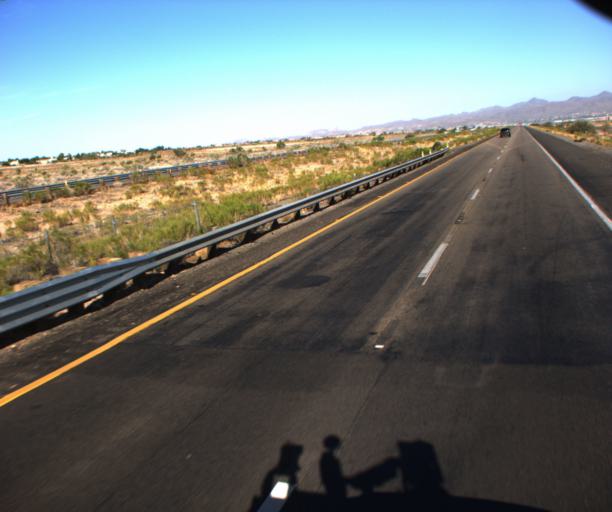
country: US
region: Arizona
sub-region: Mohave County
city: New Kingman-Butler
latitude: 35.2072
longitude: -113.9525
